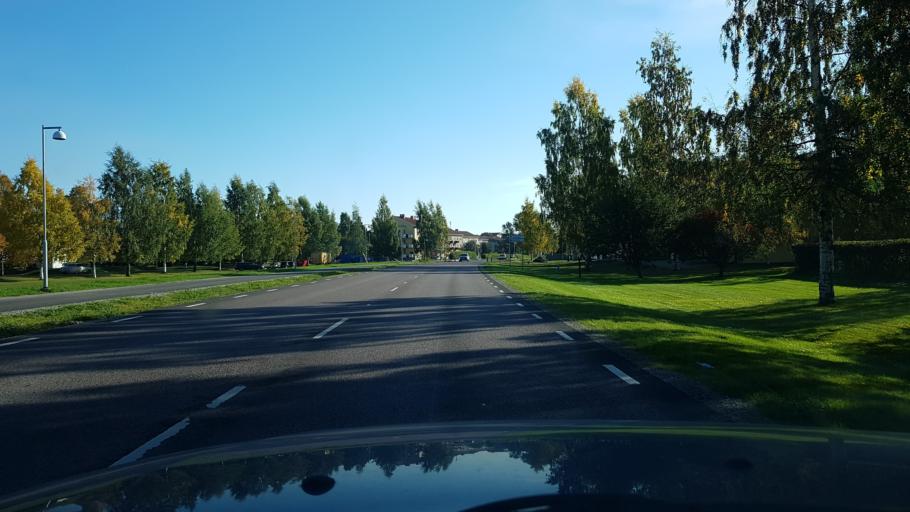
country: SE
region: Norrbotten
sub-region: Pitea Kommun
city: Pitea
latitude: 65.3230
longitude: 21.4616
